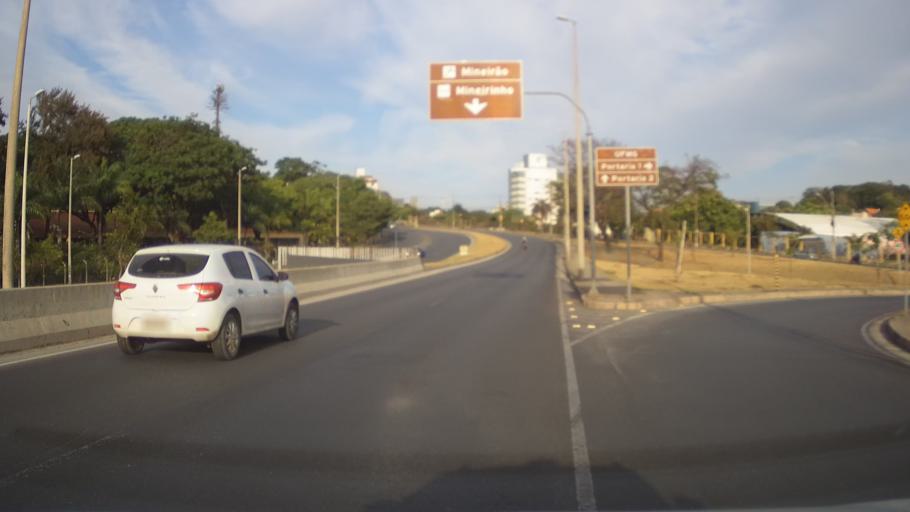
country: BR
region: Minas Gerais
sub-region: Belo Horizonte
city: Belo Horizonte
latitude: -19.8601
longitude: -43.9597
